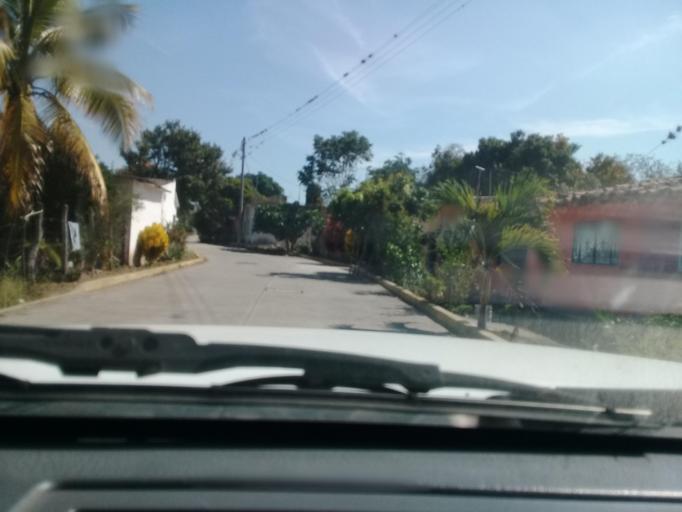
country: MX
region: Veracruz
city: Actopan
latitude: 19.4804
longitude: -96.6461
